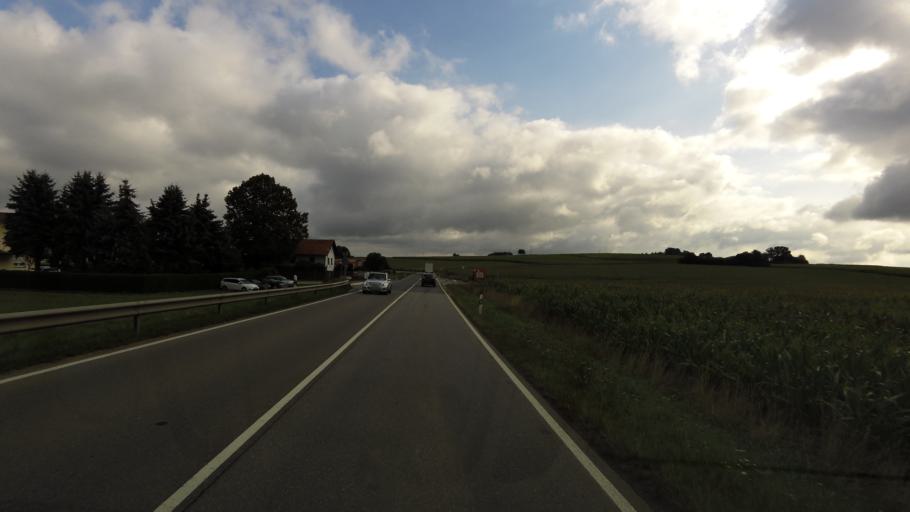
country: DE
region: Bavaria
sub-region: Upper Palatinate
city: Cham
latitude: 49.1886
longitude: 12.6536
